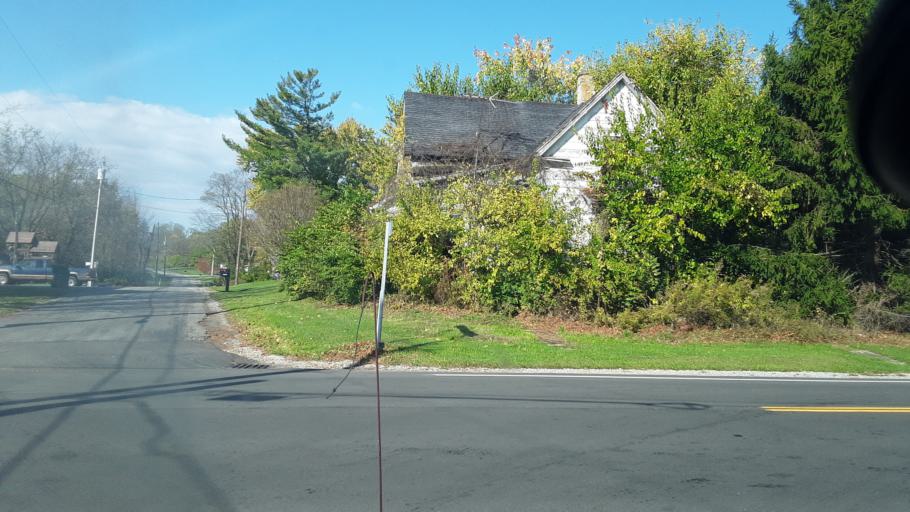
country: US
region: Ohio
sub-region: Highland County
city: Leesburg
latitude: 39.2832
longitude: -83.5925
